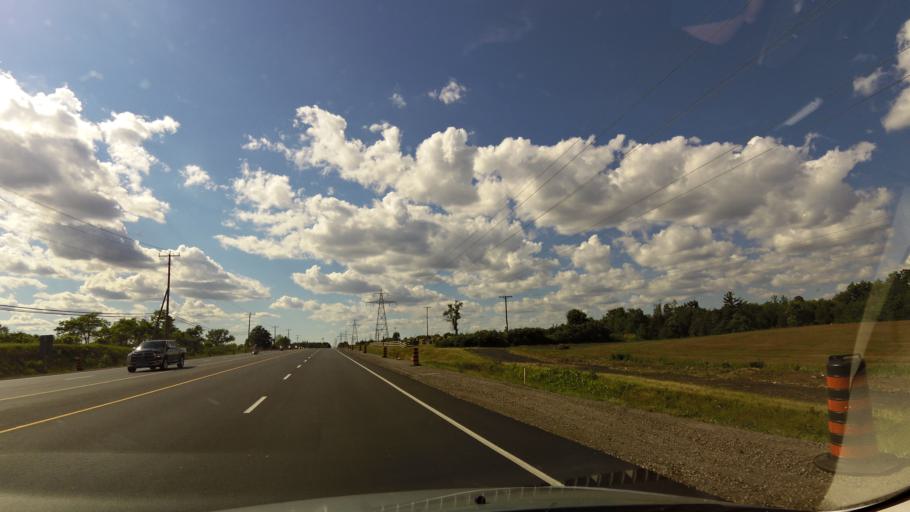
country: CA
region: Ontario
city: Ancaster
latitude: 43.3900
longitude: -80.0234
